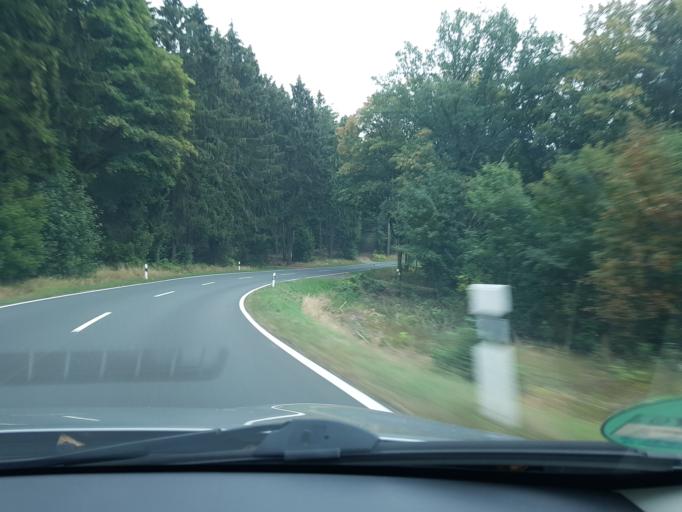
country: DE
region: Rheinland-Pfalz
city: Becheln
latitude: 50.2882
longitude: 7.7284
